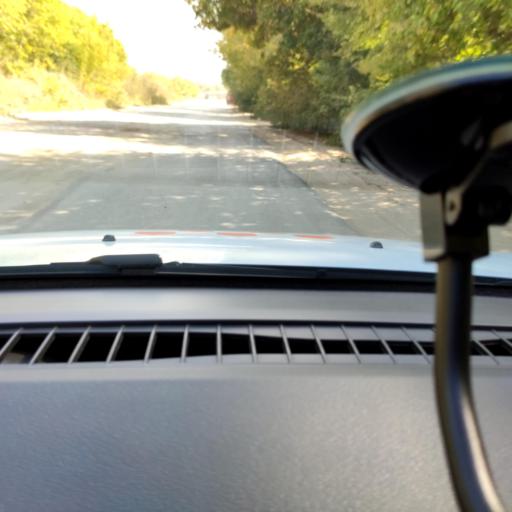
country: RU
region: Samara
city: Samara
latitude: 53.1814
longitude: 50.2645
